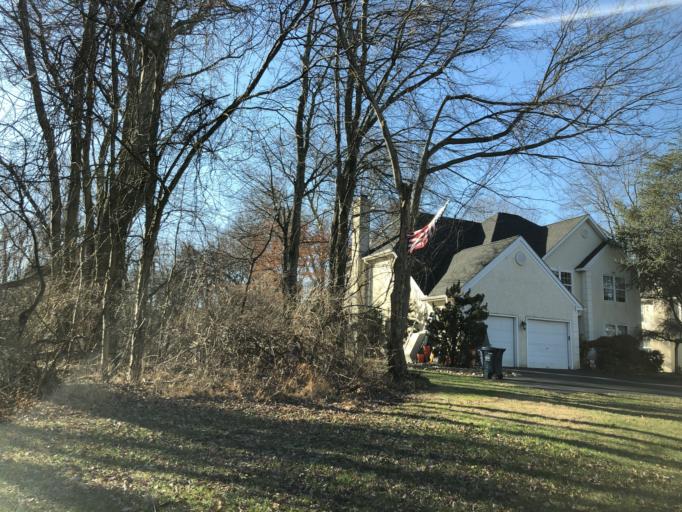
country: US
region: Pennsylvania
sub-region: Delaware County
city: Chester Heights
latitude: 39.8571
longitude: -75.4683
